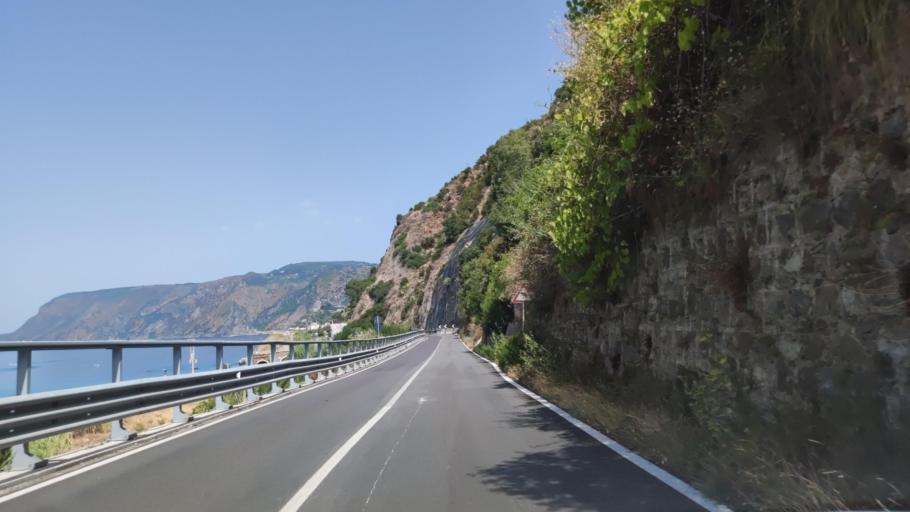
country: IT
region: Calabria
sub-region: Provincia di Reggio Calabria
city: Bagnara Calabra
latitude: 38.2759
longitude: 15.7868
